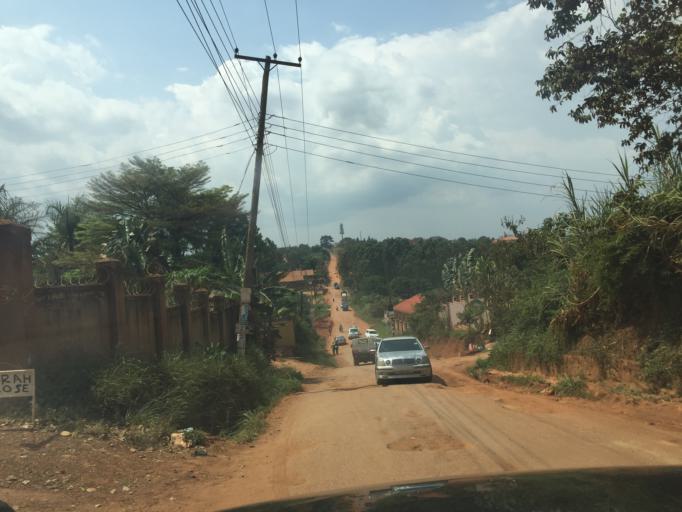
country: UG
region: Central Region
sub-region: Wakiso District
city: Kireka
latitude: 0.3927
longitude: 32.6248
